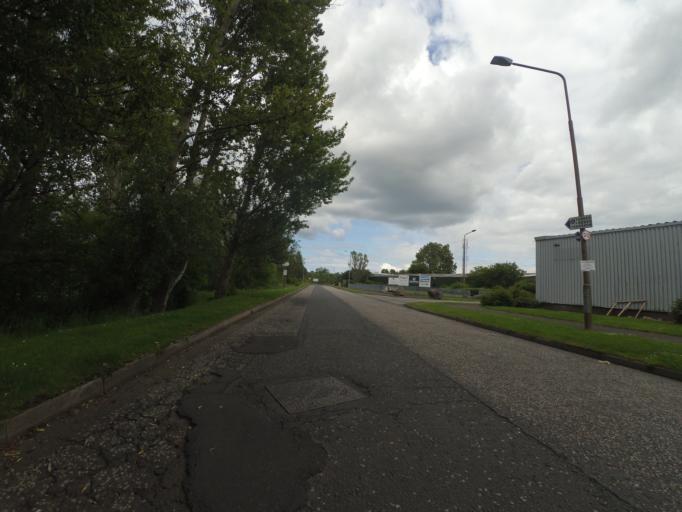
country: GB
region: Scotland
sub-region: West Lothian
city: Seafield
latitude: 55.9343
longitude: -3.1481
